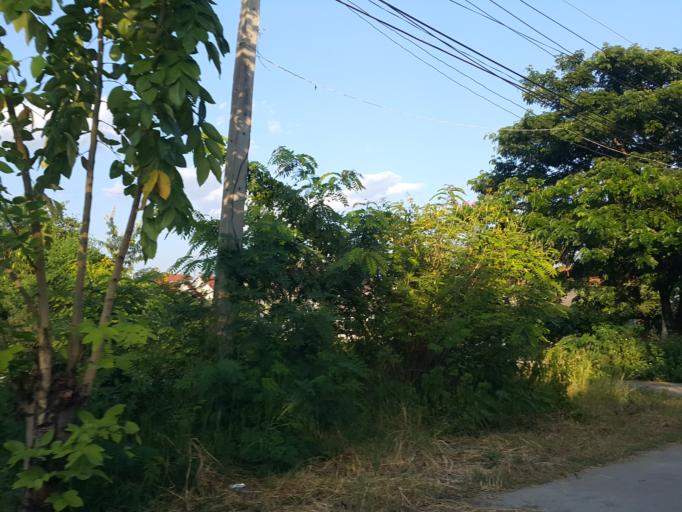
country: TH
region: Chiang Mai
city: San Kamphaeng
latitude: 18.7486
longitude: 99.1154
